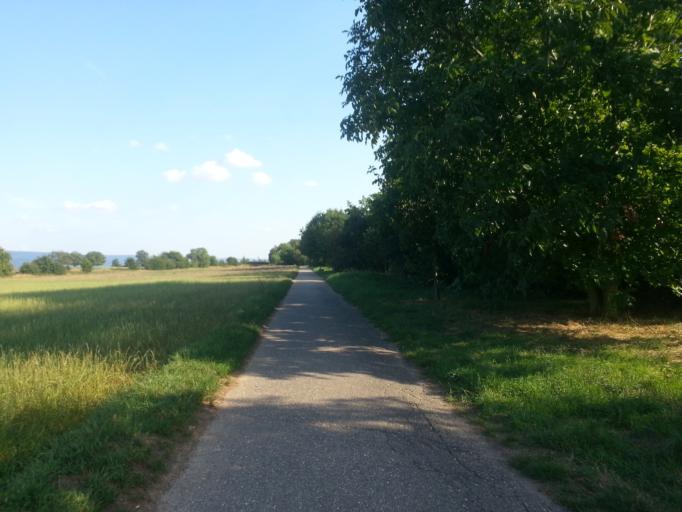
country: DE
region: Baden-Wuerttemberg
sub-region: Karlsruhe Region
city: Edingen-Neckarhausen
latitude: 49.4599
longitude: 8.6091
